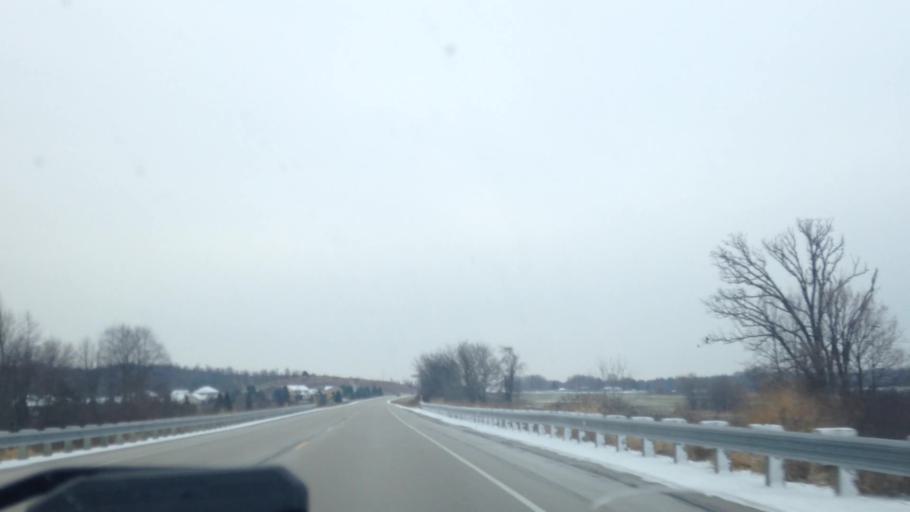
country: US
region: Wisconsin
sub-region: Waukesha County
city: Oconomowoc
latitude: 43.1732
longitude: -88.5065
